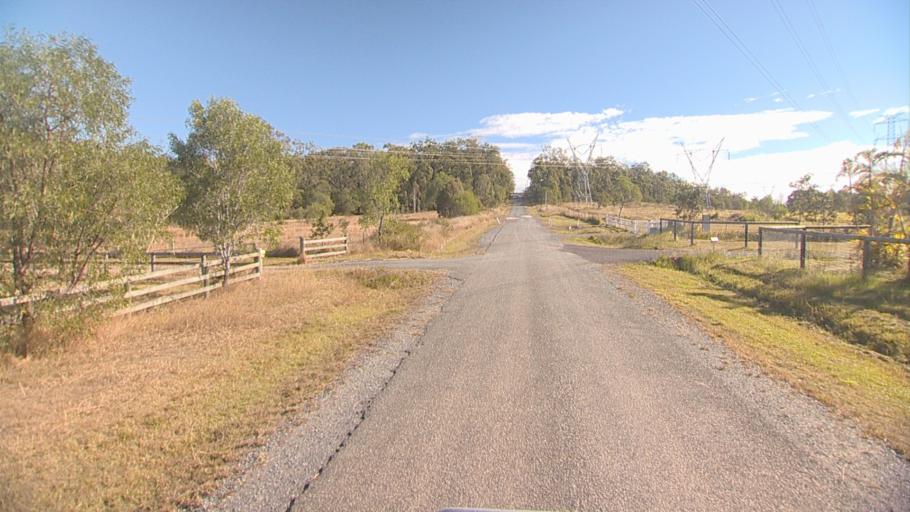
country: AU
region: Queensland
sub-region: Logan
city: Chambers Flat
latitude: -27.7968
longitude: 153.0844
